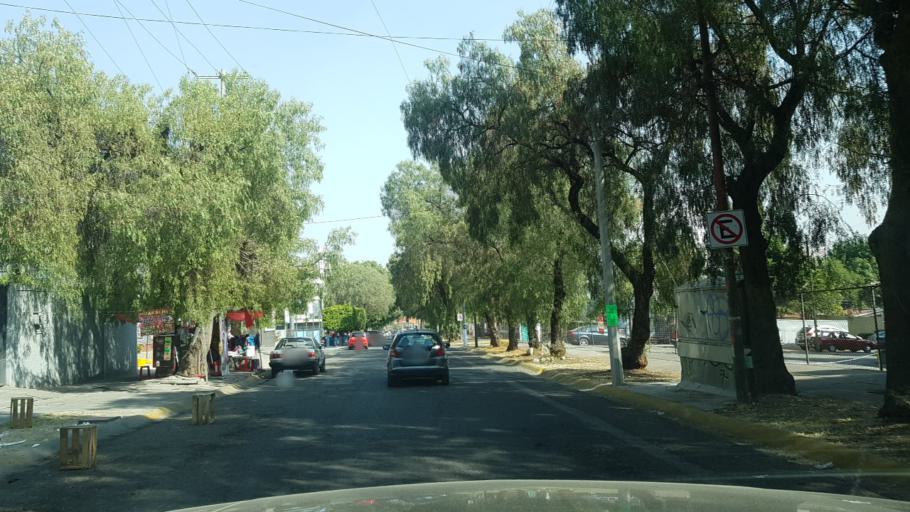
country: MX
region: Mexico
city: Cuautitlan Izcalli
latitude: 19.6505
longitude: -99.2078
